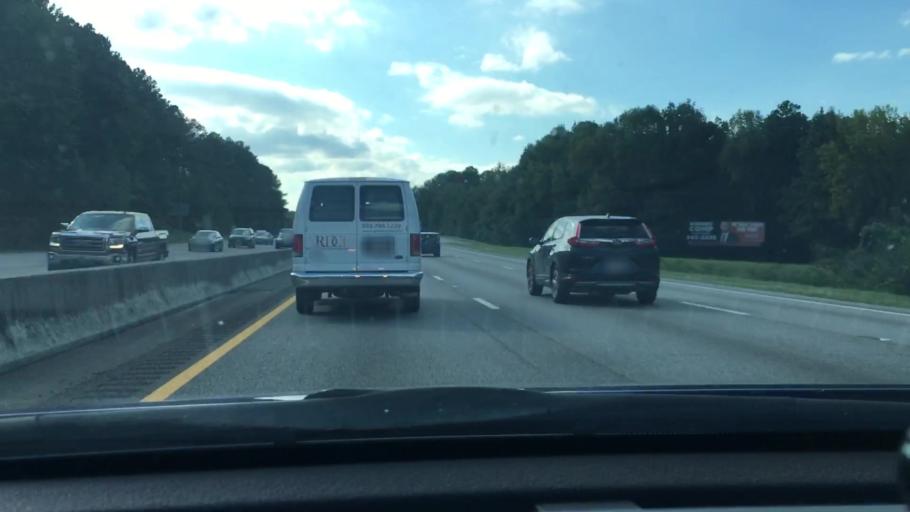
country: US
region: South Carolina
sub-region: Richland County
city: Dentsville
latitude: 34.0738
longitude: -81.0011
